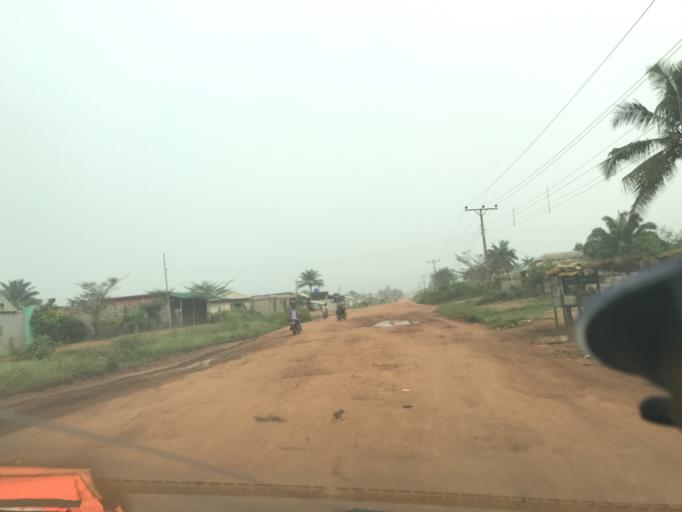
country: NG
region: Ogun
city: Ado Odo
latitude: 6.5332
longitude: 2.9507
